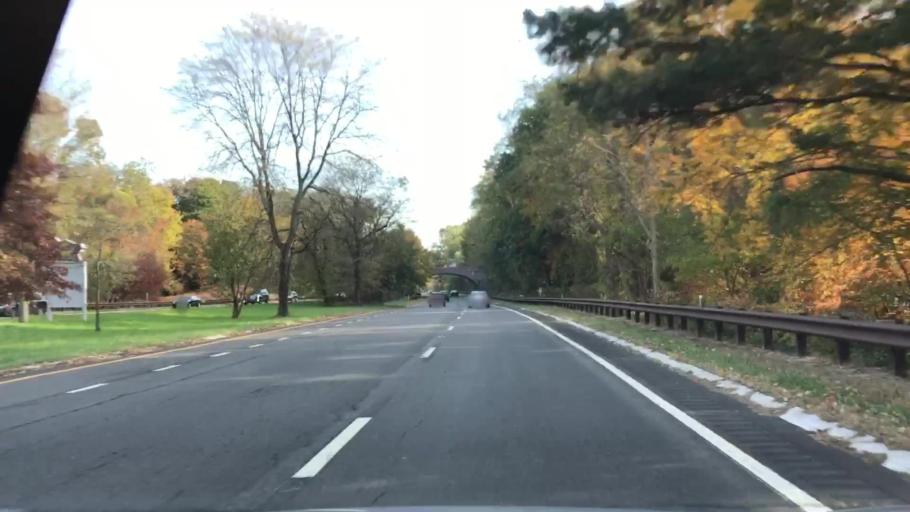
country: US
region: New York
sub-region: Rockland County
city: Tappan
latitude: 41.0247
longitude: -73.9369
